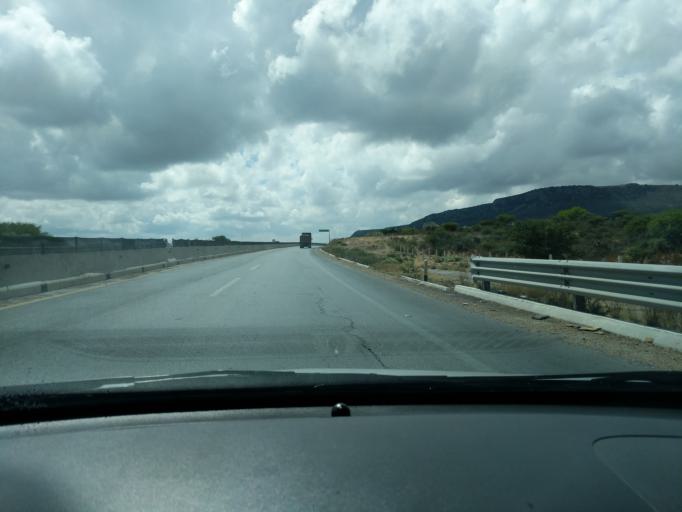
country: MX
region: Zacatecas
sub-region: Pinos
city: Santiago
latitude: 22.4067
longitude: -101.3923
